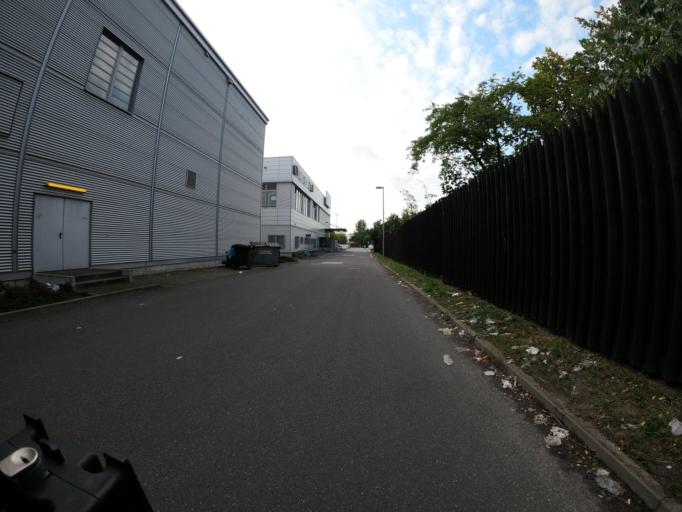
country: DE
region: Berlin
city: Siemensstadt
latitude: 52.5403
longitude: 13.2500
